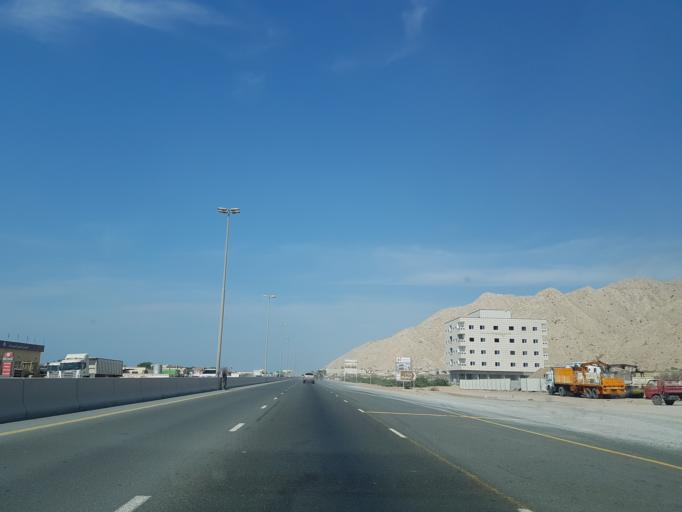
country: AE
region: Ra's al Khaymah
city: Ras al-Khaimah
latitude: 25.8479
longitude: 56.0198
